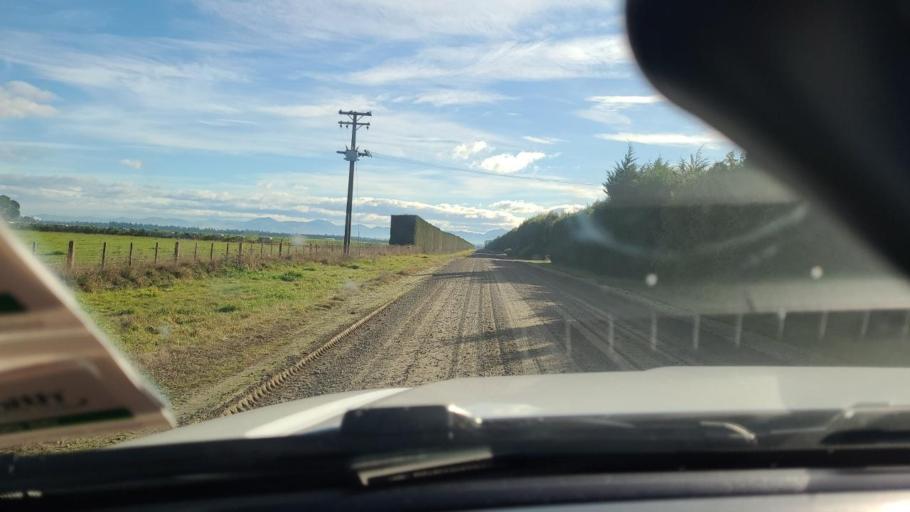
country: NZ
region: Southland
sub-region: Gore District
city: Gore
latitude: -45.9131
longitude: 168.7960
